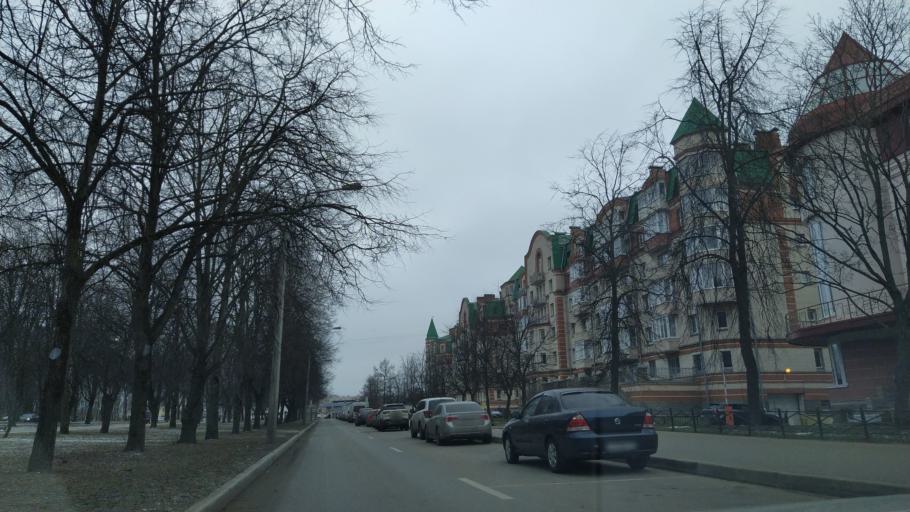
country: RU
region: St.-Petersburg
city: Pushkin
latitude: 59.7328
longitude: 30.4143
